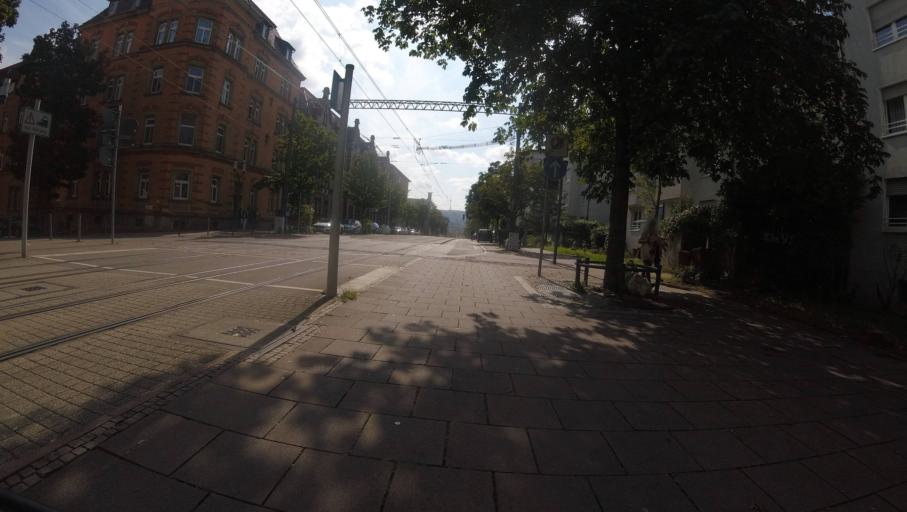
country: DE
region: Baden-Wuerttemberg
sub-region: Regierungsbezirk Stuttgart
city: Stuttgart
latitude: 48.7965
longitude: 9.1900
